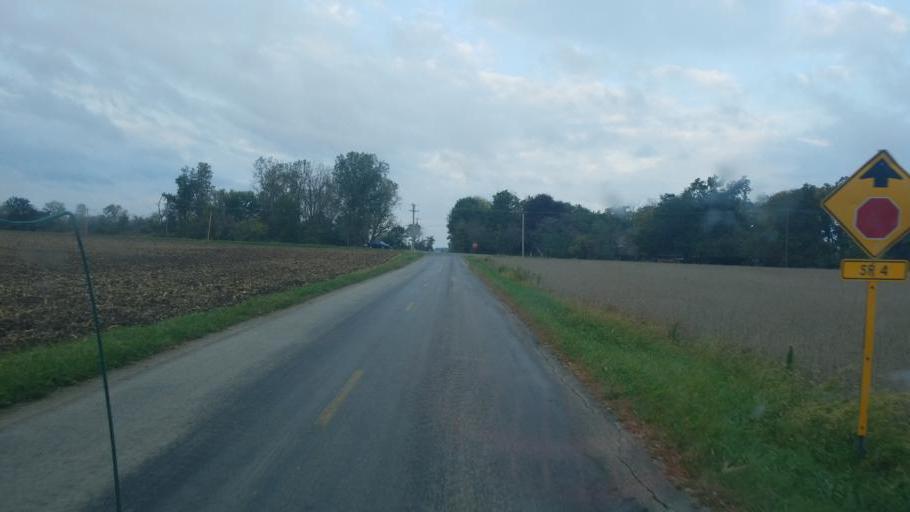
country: US
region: Ohio
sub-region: Marion County
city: Marion
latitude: 40.6739
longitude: -83.1020
